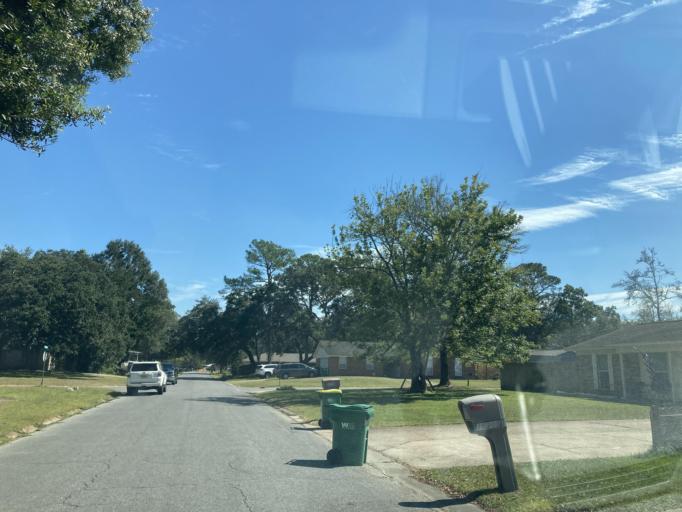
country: US
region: Mississippi
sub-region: Jackson County
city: Saint Martin
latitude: 30.4505
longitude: -88.8801
